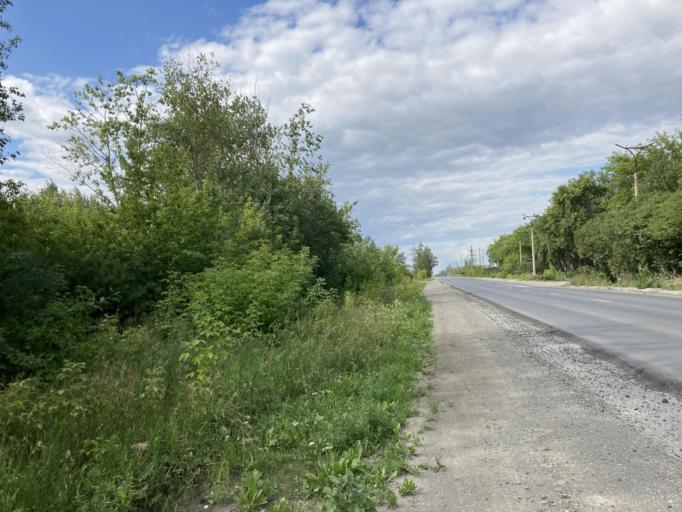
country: RU
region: Sverdlovsk
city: Bogdanovich
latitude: 56.7978
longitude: 62.0400
